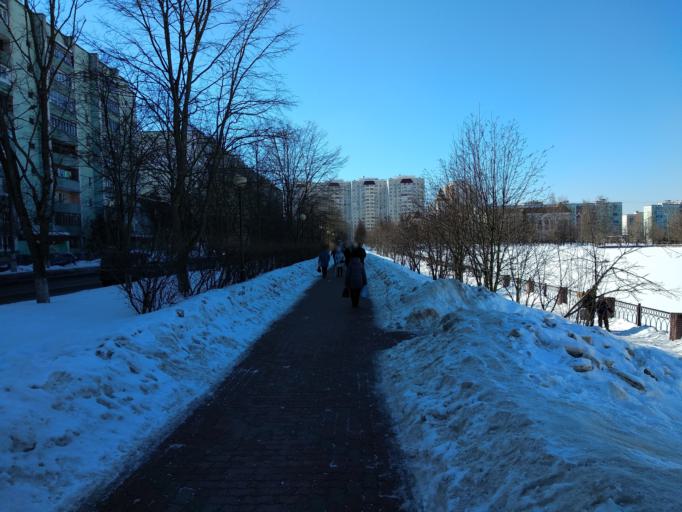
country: RU
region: Moskovskaya
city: Krasnoznamensk
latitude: 55.6003
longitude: 37.0411
